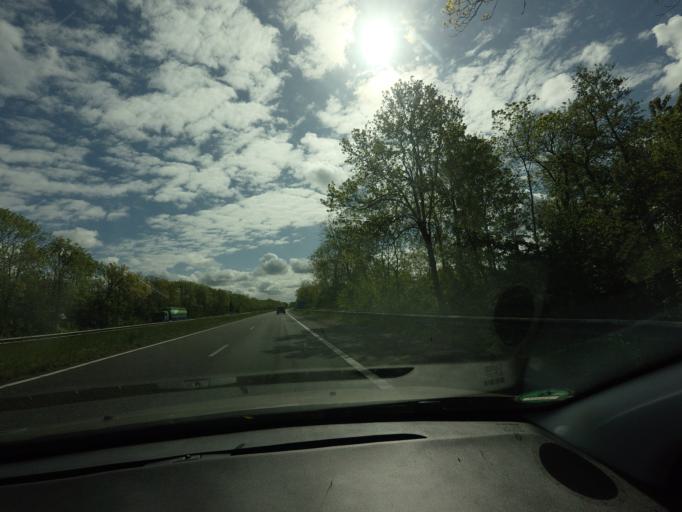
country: NL
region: Friesland
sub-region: Sudwest Fryslan
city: Bolsward
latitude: 53.0578
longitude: 5.5230
